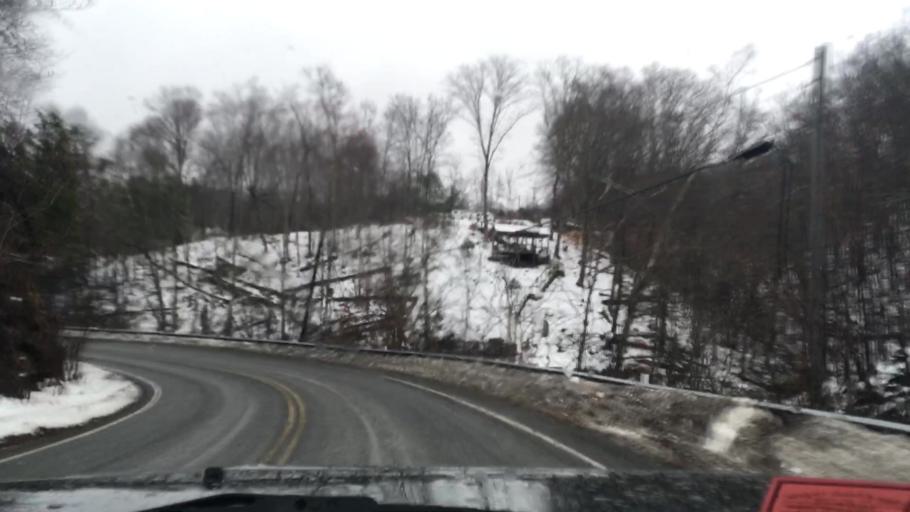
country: US
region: Virginia
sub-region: Pulaski County
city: Dublin
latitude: 37.0010
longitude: -80.6803
